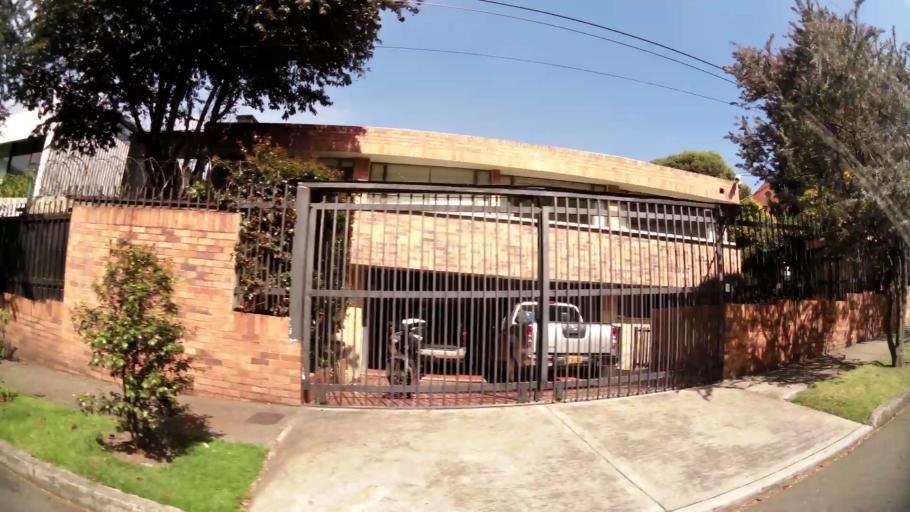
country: CO
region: Bogota D.C.
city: Barrio San Luis
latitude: 4.6923
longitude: -74.0299
